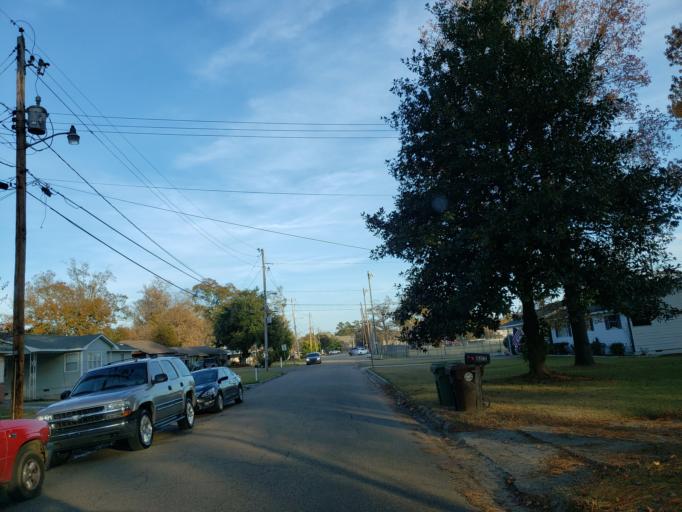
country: US
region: Mississippi
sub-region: Forrest County
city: Hattiesburg
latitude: 31.3284
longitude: -89.3128
